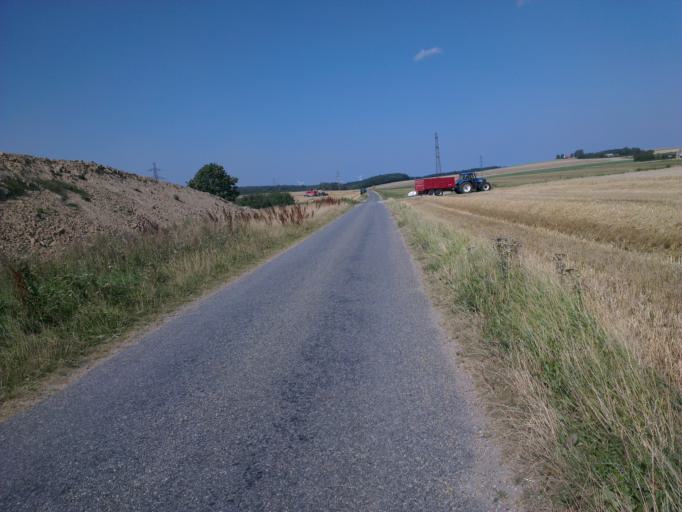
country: DK
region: Capital Region
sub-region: Frederikssund Kommune
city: Skibby
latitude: 55.8025
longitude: 11.9082
